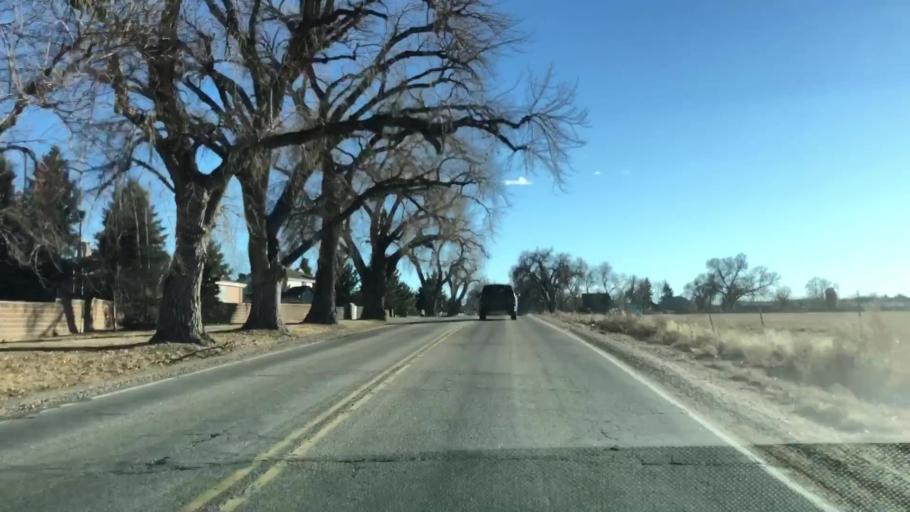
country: US
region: Colorado
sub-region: Weld County
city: Windsor
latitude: 40.4837
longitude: -104.9820
